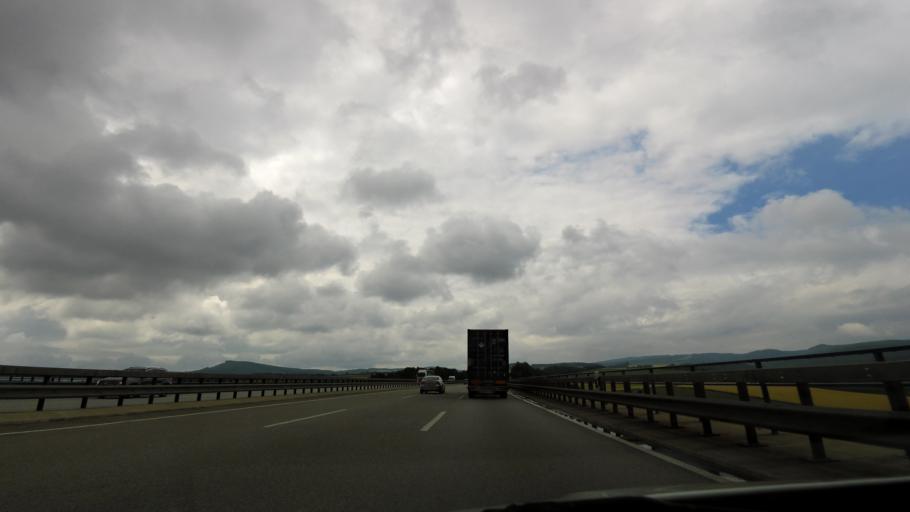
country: DE
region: Rheinland-Pfalz
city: Niederzissen
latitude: 50.4622
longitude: 7.2339
